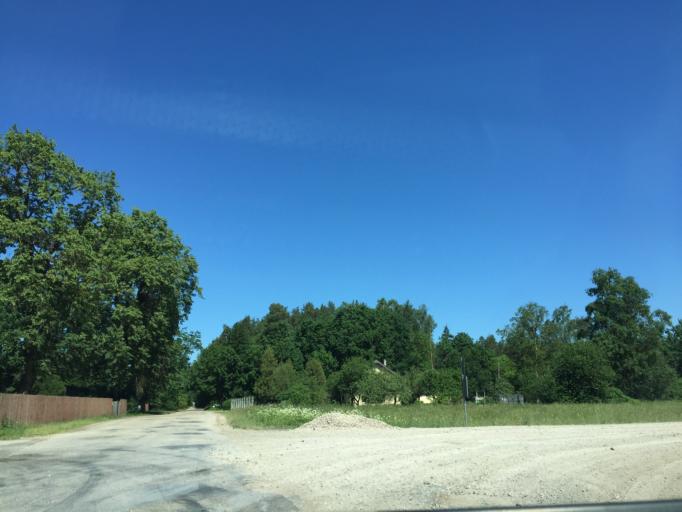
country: LV
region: Marupe
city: Marupe
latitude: 56.8840
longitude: 23.9768
